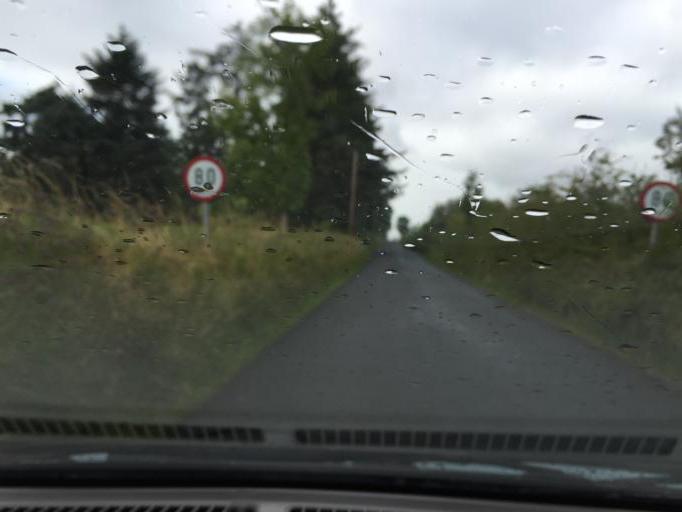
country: IE
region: Connaught
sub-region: Sligo
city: Tobercurry
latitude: 54.0383
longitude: -8.8473
